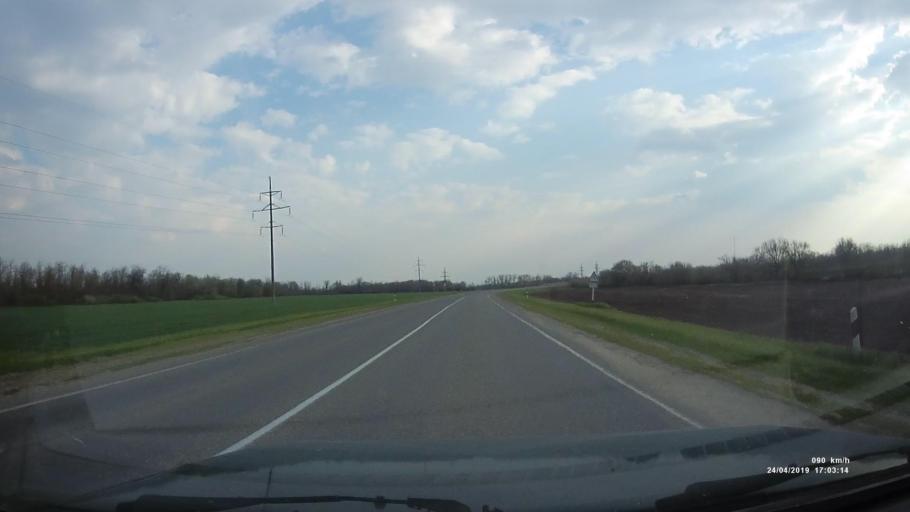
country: RU
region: Rostov
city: Sal'sk
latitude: 46.5685
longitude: 41.6126
